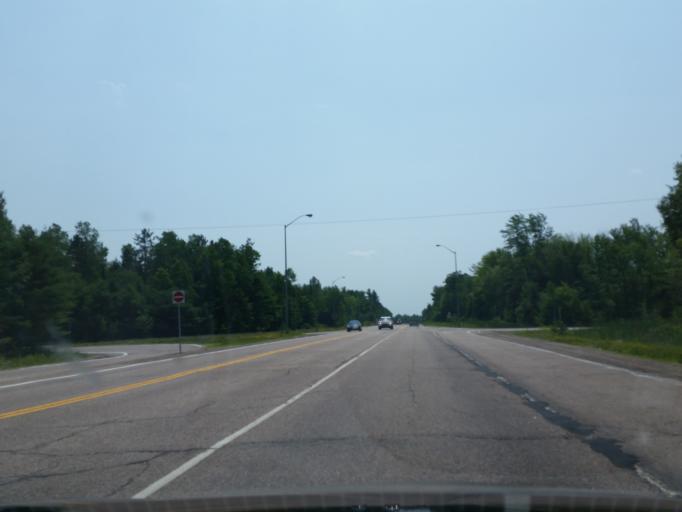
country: CA
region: Ontario
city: Petawawa
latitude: 45.8812
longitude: -77.3039
